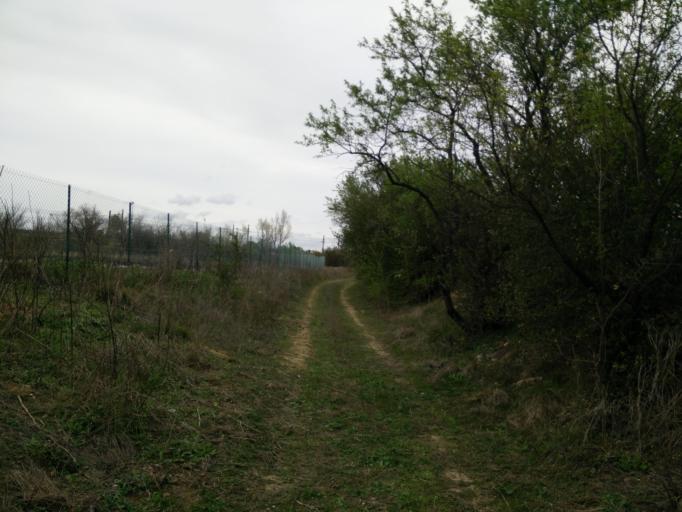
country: FR
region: Languedoc-Roussillon
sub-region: Departement du Gard
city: Gallargues-le-Montueux
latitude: 43.7123
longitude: 4.1688
